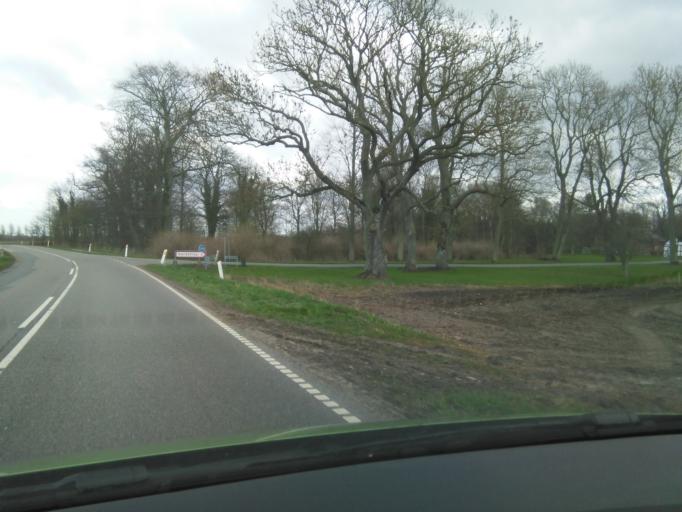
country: DK
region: South Denmark
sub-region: Nordfyns Kommune
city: Bogense
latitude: 55.5667
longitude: 10.1460
